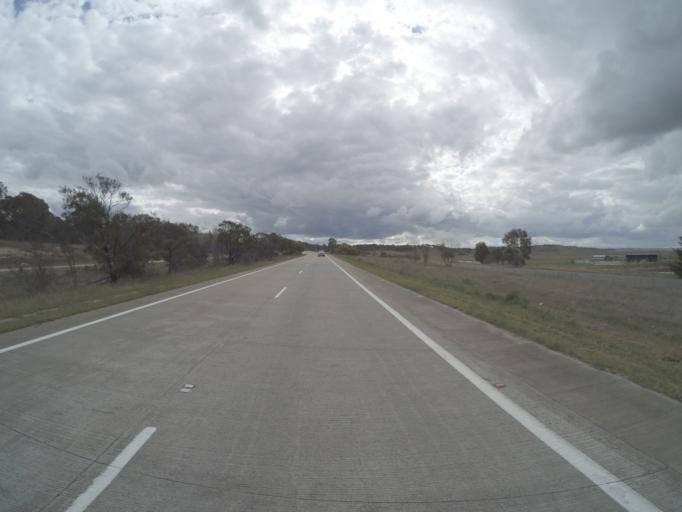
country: AU
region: New South Wales
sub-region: Goulburn Mulwaree
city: Goulburn
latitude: -34.8046
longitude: 149.5131
